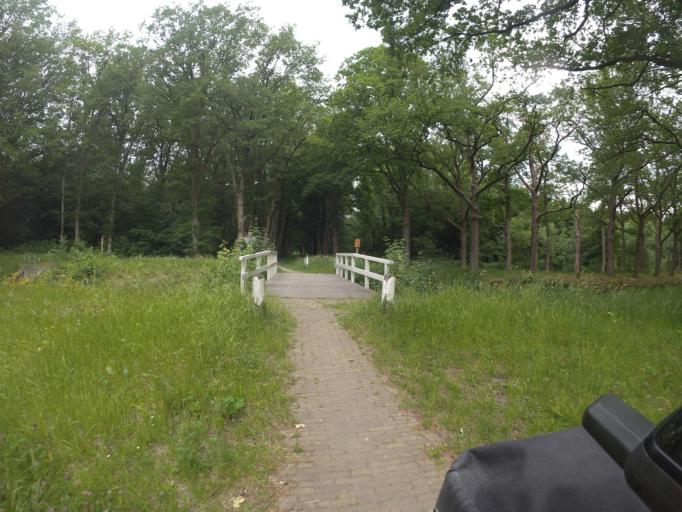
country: NL
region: Groningen
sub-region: Gemeente Leek
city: Leek
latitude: 53.0192
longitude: 6.4150
